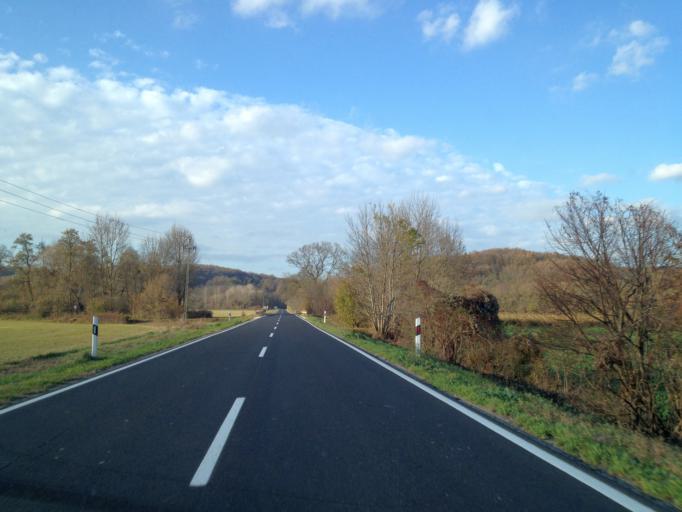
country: HU
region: Gyor-Moson-Sopron
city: Bakonyszentlaszlo
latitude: 47.3819
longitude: 17.8701
